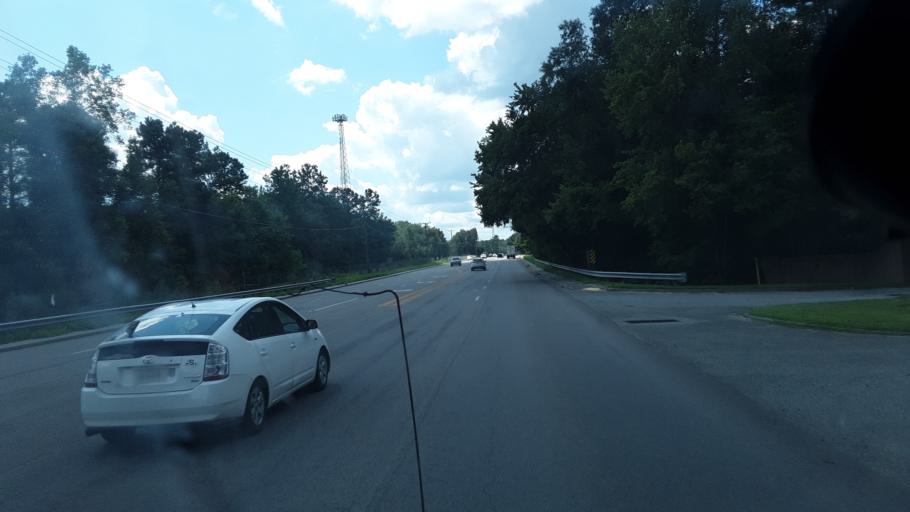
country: US
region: South Carolina
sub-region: Berkeley County
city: Sangaree
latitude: 33.0792
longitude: -80.0842
